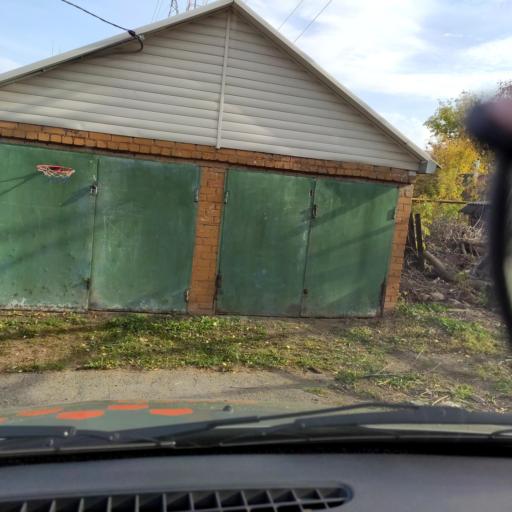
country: RU
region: Bashkortostan
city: Ufa
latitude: 54.7234
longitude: 55.9209
